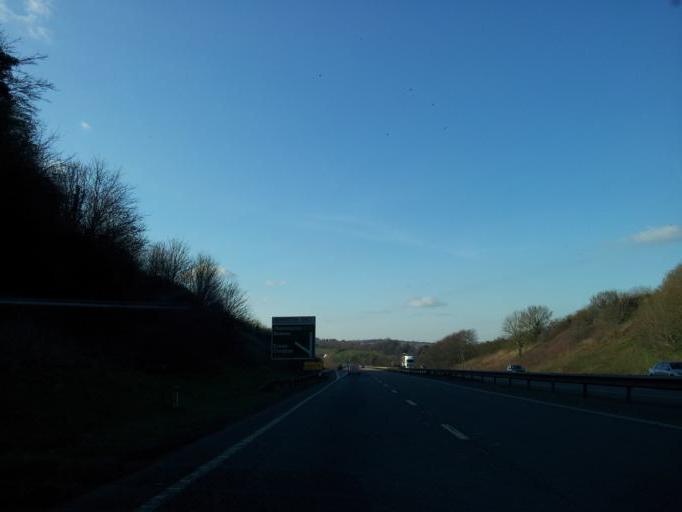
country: GB
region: England
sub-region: Devon
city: Exeter
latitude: 50.6963
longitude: -3.5412
